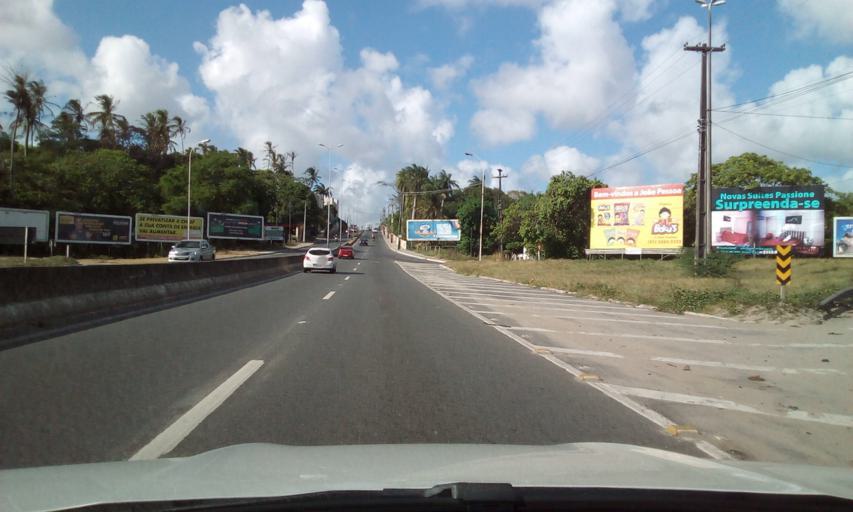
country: BR
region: Paraiba
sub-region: Bayeux
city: Bayeux
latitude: -7.1648
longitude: -34.8965
